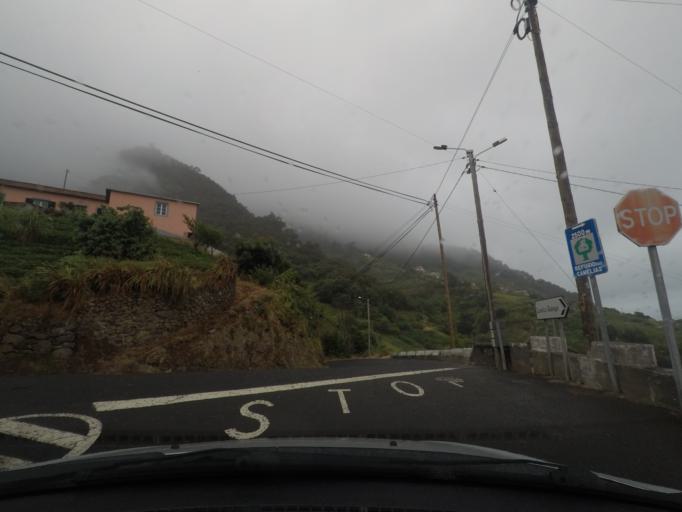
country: PT
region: Madeira
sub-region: Santana
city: Santana
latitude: 32.7848
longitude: -16.8571
